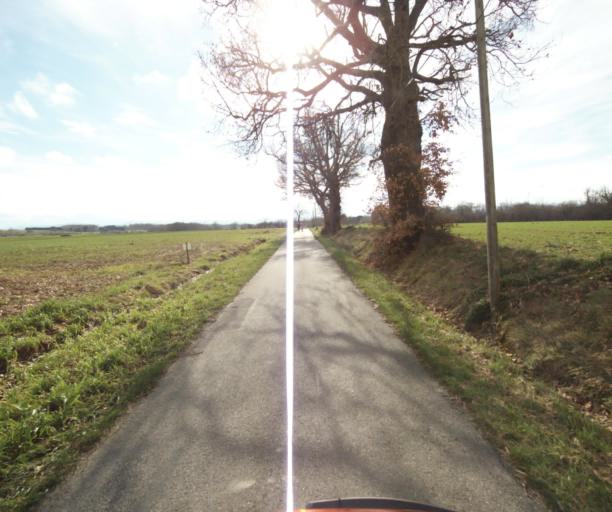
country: FR
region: Midi-Pyrenees
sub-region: Departement de l'Ariege
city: La Tour-du-Crieu
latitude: 43.1235
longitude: 1.6936
